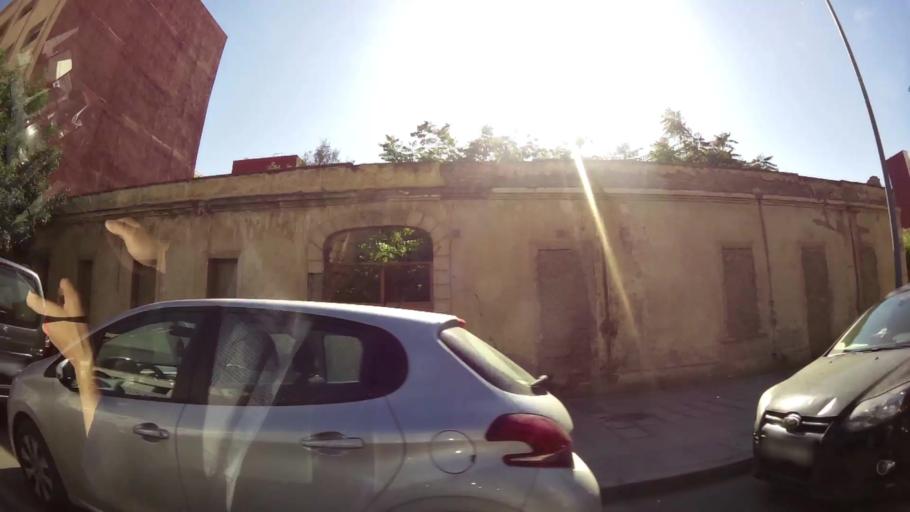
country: MA
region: Oriental
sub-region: Oujda-Angad
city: Oujda
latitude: 34.6879
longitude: -1.9170
